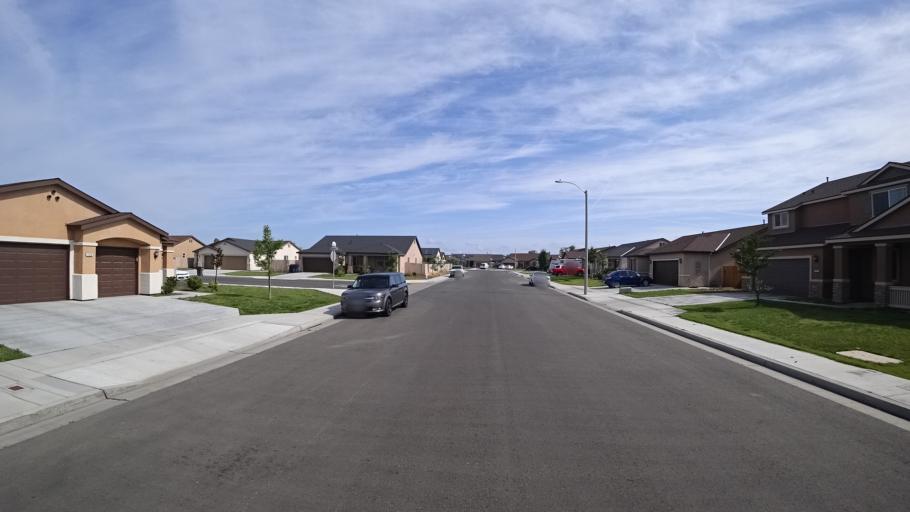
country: US
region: California
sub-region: Kings County
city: Hanford
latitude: 36.3077
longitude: -119.6685
